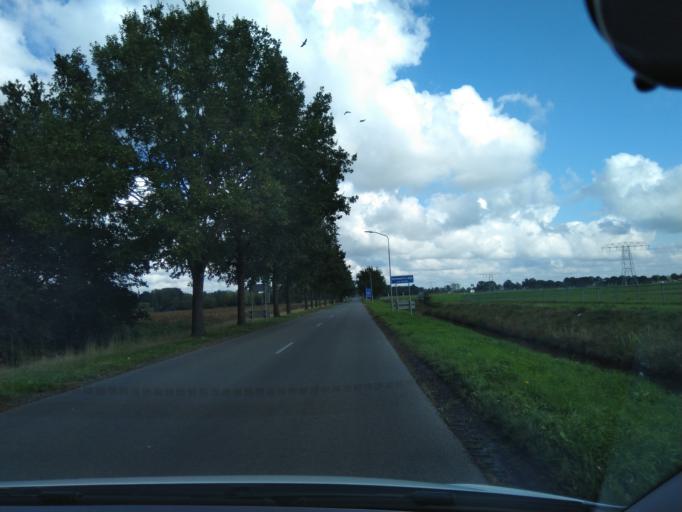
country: NL
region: Groningen
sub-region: Gemeente Veendam
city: Veendam
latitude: 53.0883
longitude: 6.9071
